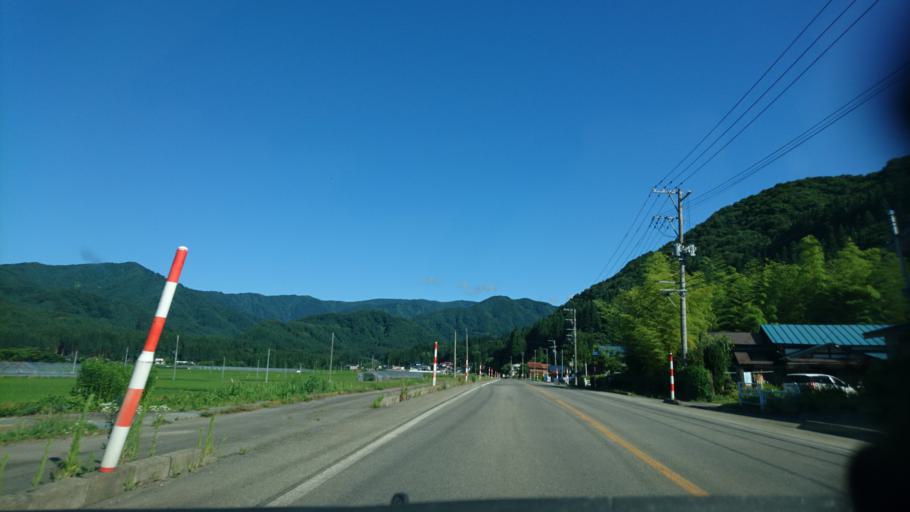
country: JP
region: Akita
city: Kakunodatemachi
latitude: 39.6779
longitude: 140.5645
